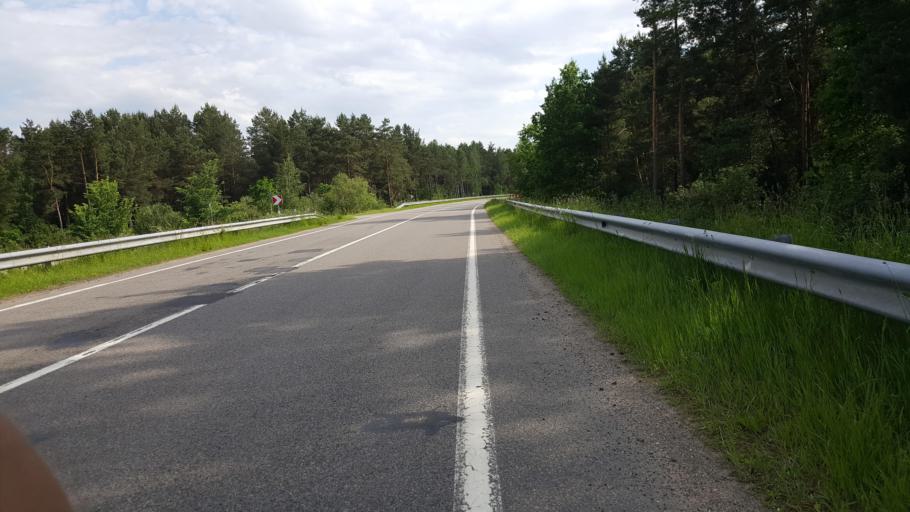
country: BY
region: Brest
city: Zhabinka
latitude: 52.4722
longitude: 24.1551
